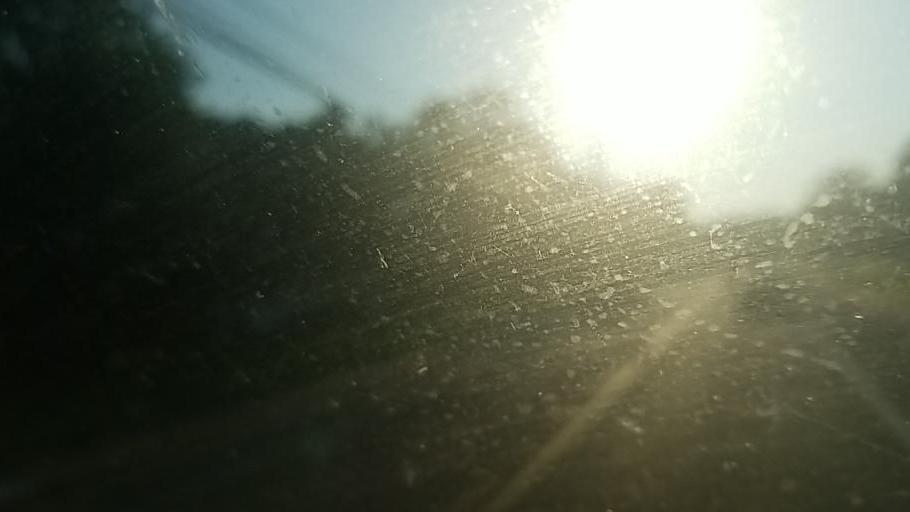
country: US
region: Delaware
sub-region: Sussex County
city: Selbyville
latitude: 38.4565
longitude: -75.2155
